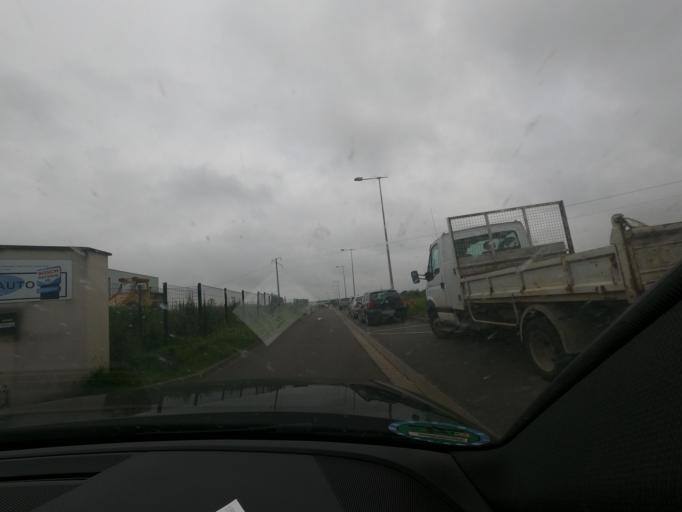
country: FR
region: Picardie
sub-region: Departement de l'Oise
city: Ressons-sur-Matz
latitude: 49.5359
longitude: 2.7374
